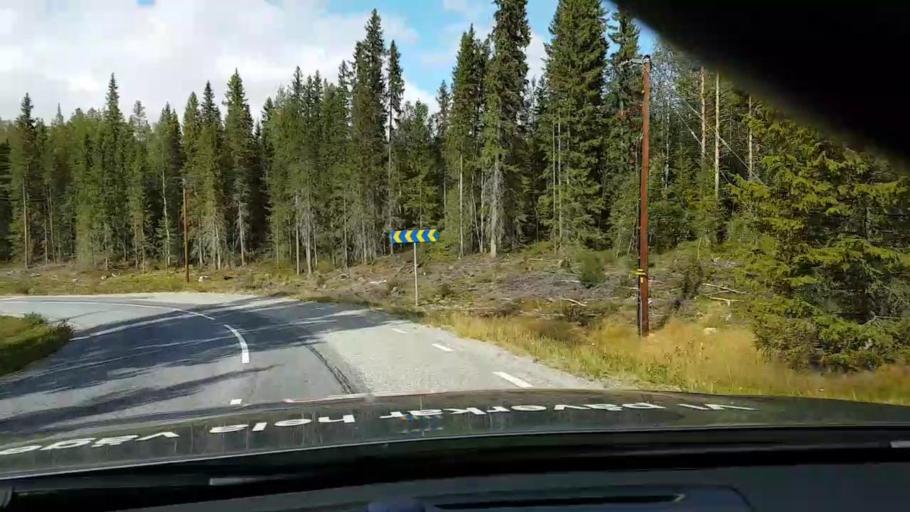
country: SE
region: Vaesterbotten
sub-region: Asele Kommun
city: Asele
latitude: 63.8444
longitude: 17.4230
